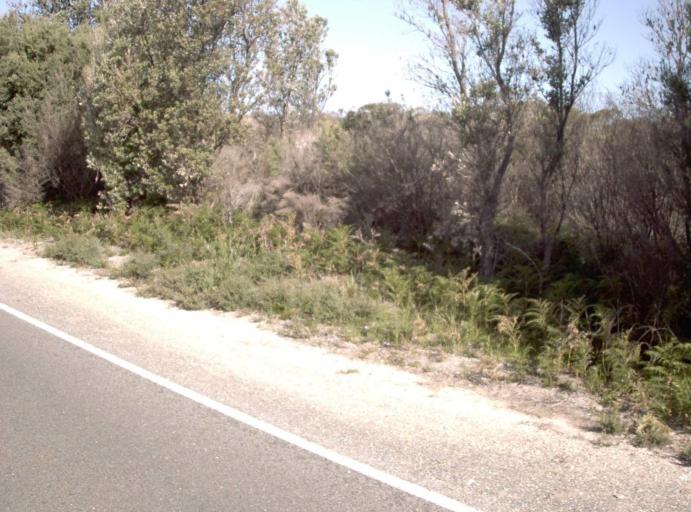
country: AU
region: Victoria
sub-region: East Gippsland
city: Lakes Entrance
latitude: -37.8019
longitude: 148.7278
